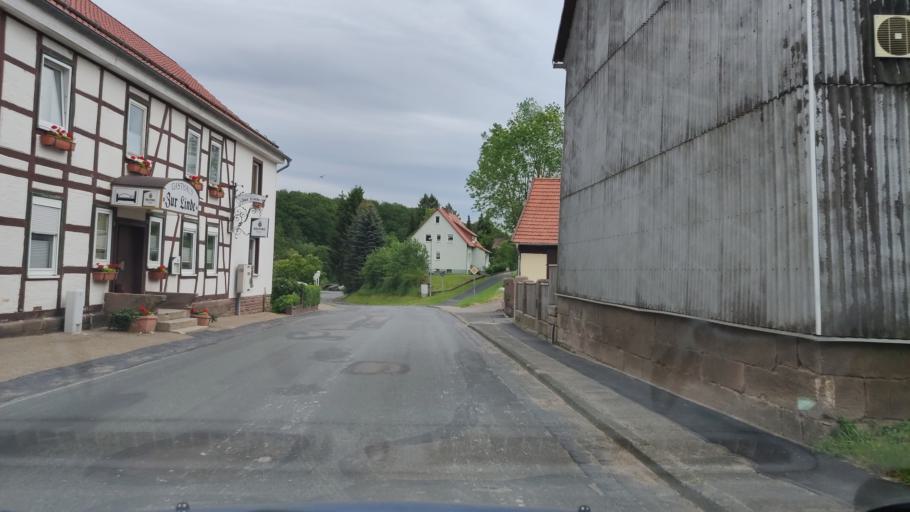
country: DE
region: Lower Saxony
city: Hardegsen
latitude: 51.6831
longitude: 9.8110
